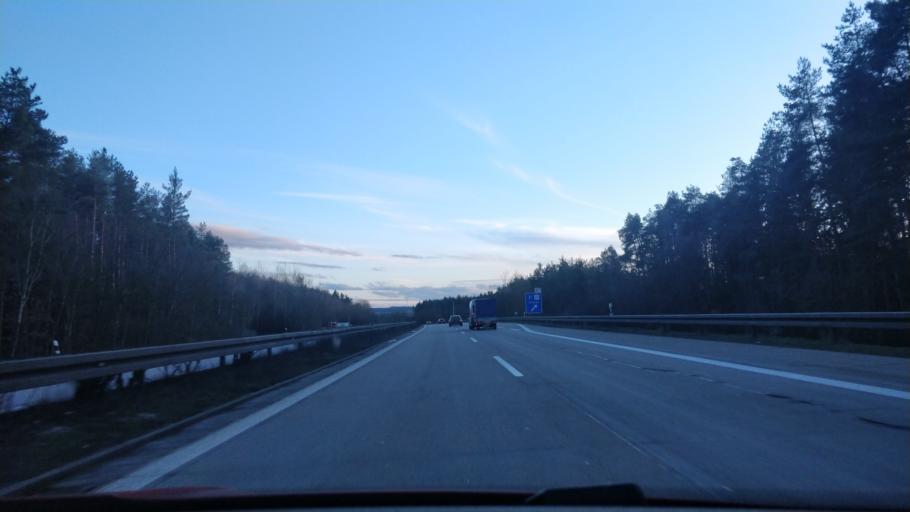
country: DE
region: Bavaria
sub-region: Upper Palatinate
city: Luhe-Wildenau
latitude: 49.5747
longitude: 12.1241
